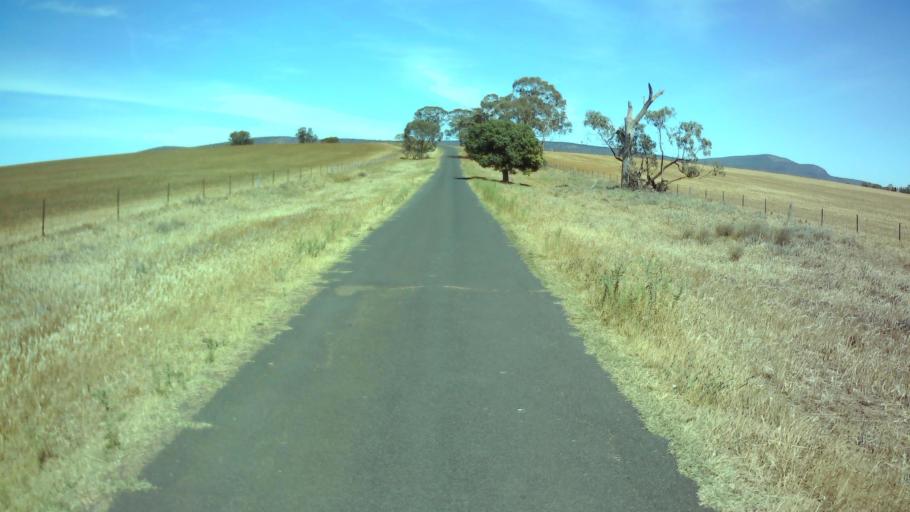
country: AU
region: New South Wales
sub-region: Weddin
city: Grenfell
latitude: -33.9410
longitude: 148.0731
